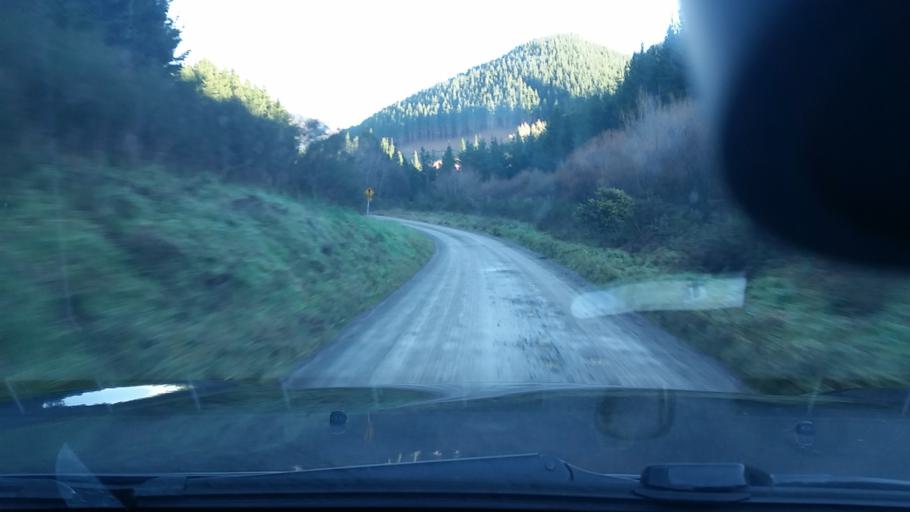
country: NZ
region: Marlborough
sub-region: Marlborough District
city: Blenheim
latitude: -41.6109
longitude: 173.9709
